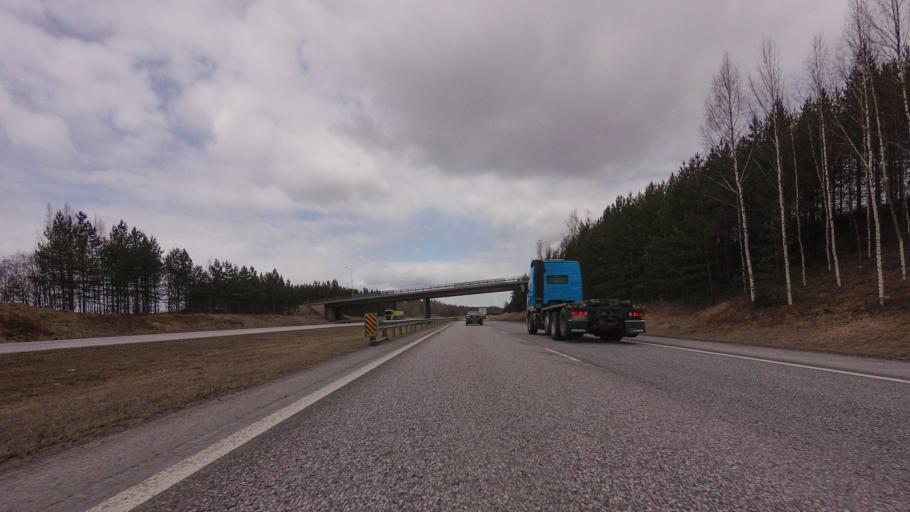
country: FI
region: Uusimaa
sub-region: Helsinki
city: Nurmijaervi
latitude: 60.3945
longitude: 24.8149
